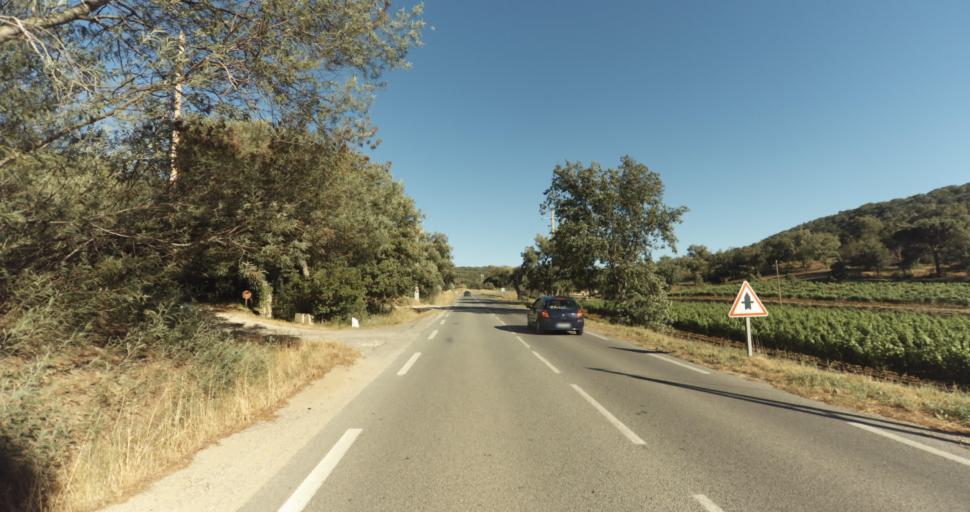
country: FR
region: Provence-Alpes-Cote d'Azur
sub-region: Departement du Var
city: Ramatuelle
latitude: 43.2369
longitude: 6.6087
